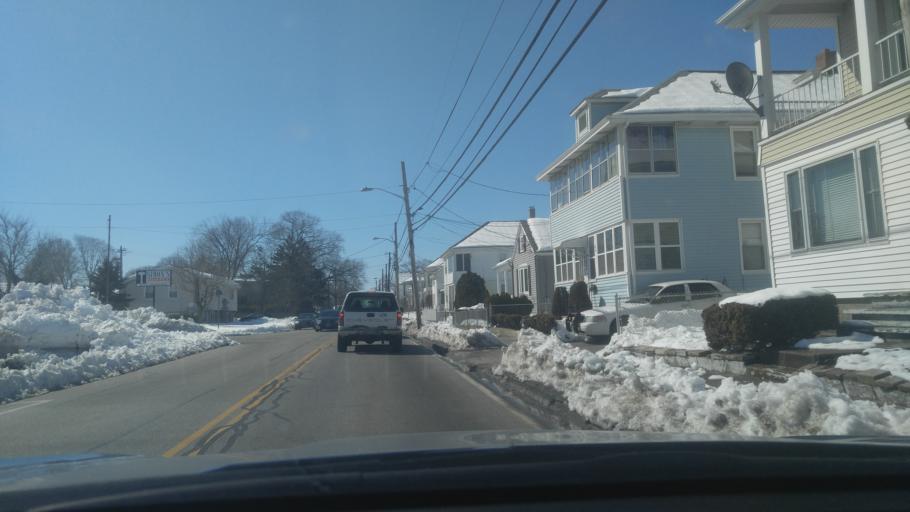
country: US
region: Massachusetts
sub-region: Bristol County
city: North Seekonk
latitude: 41.8921
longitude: -71.3578
